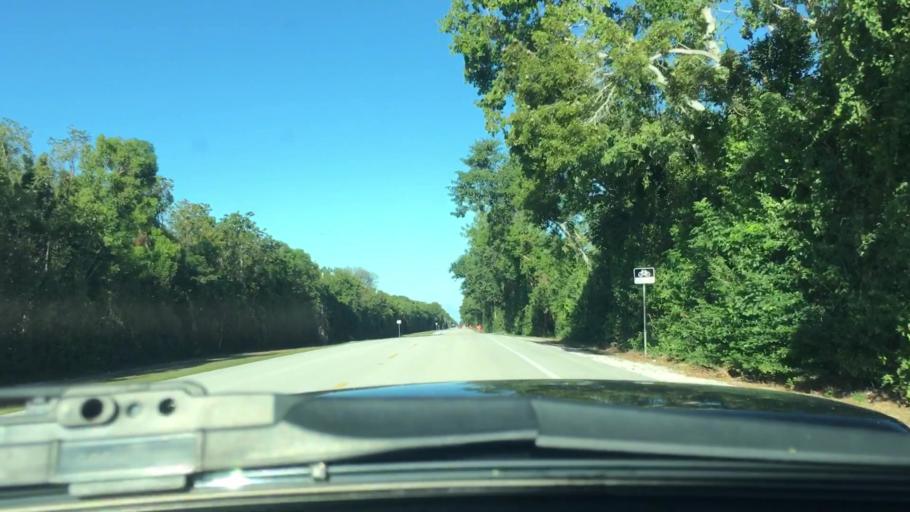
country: US
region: Florida
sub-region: Monroe County
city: North Key Largo
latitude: 25.1787
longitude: -80.3675
